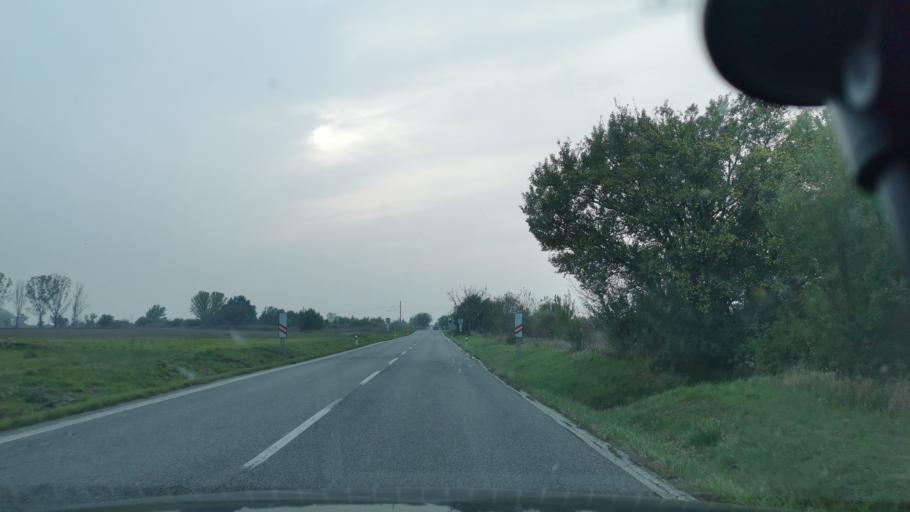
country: SK
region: Trnavsky
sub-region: Okres Skalica
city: Holic
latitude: 48.7962
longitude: 17.1386
